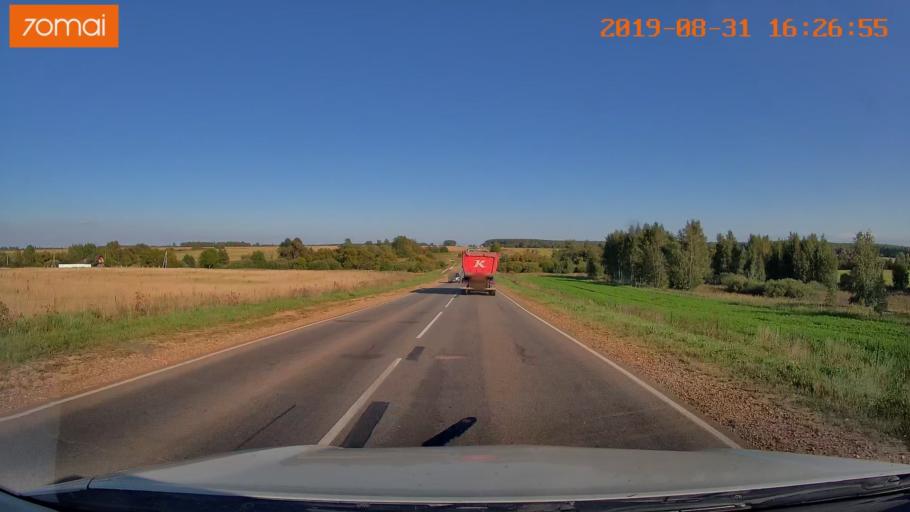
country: RU
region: Kaluga
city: Babynino
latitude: 54.5150
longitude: 35.7442
